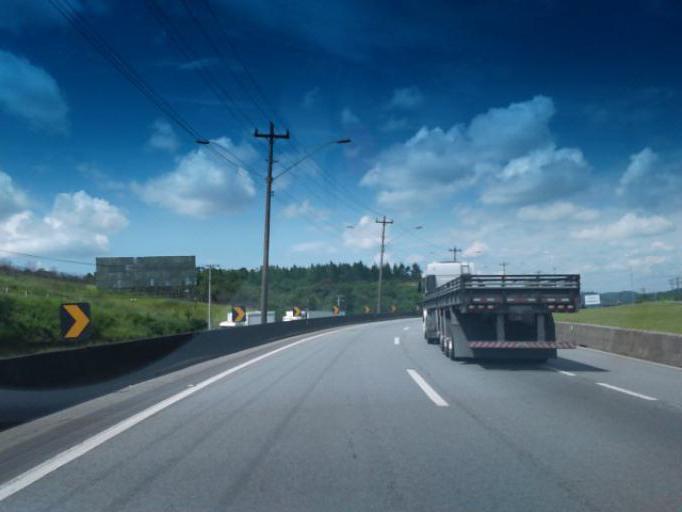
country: BR
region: Sao Paulo
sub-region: Sao Lourenco Da Serra
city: Sao Lourenco da Serra
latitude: -23.8027
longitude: -46.9182
